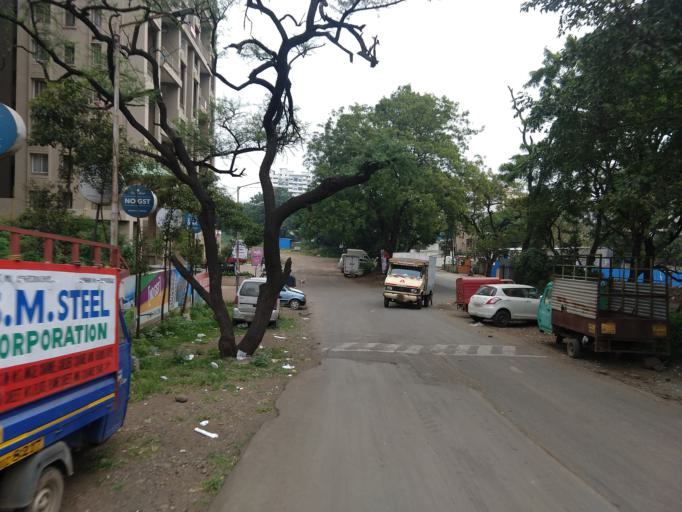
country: IN
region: Maharashtra
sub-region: Pune Division
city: Pune
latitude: 18.4553
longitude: 73.8841
